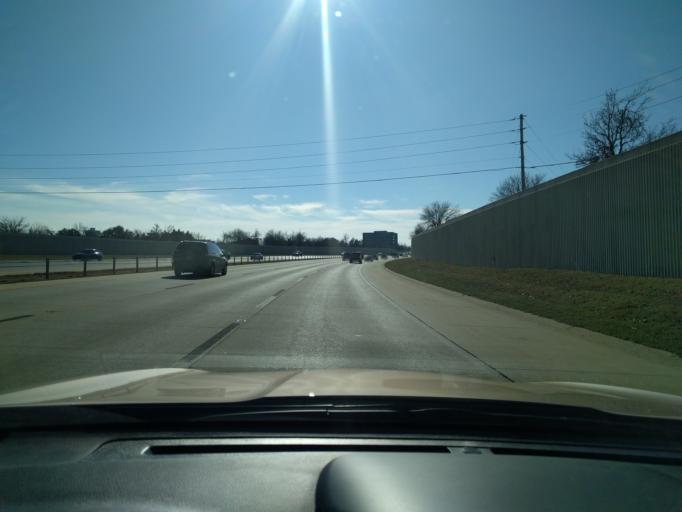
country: US
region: Oklahoma
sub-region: Oklahoma County
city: Nichols Hills
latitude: 35.5432
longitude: -97.5755
